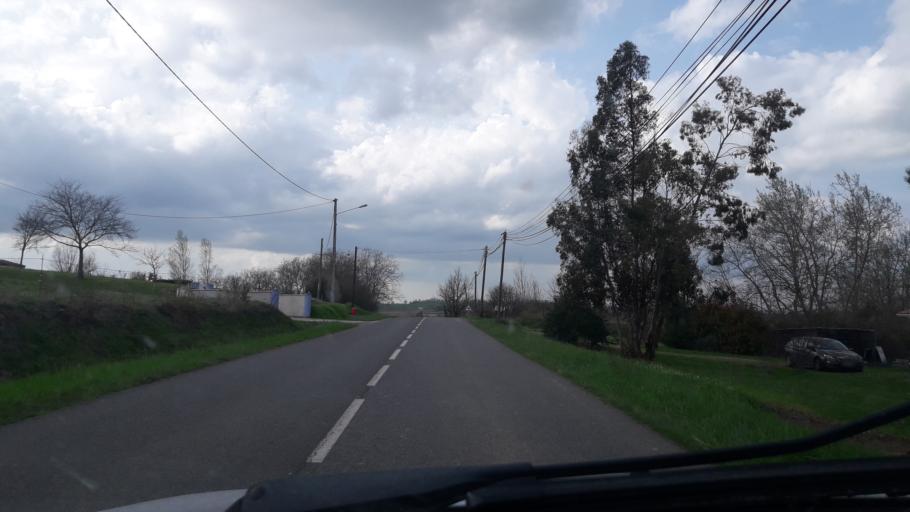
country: FR
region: Midi-Pyrenees
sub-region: Departement de la Haute-Garonne
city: Rieux-Volvestre
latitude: 43.2640
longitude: 1.2137
